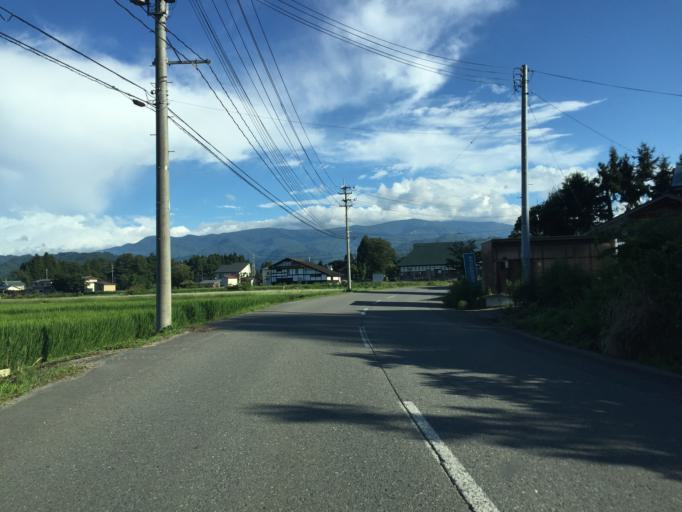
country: JP
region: Yamagata
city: Yonezawa
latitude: 37.8816
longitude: 140.0982
